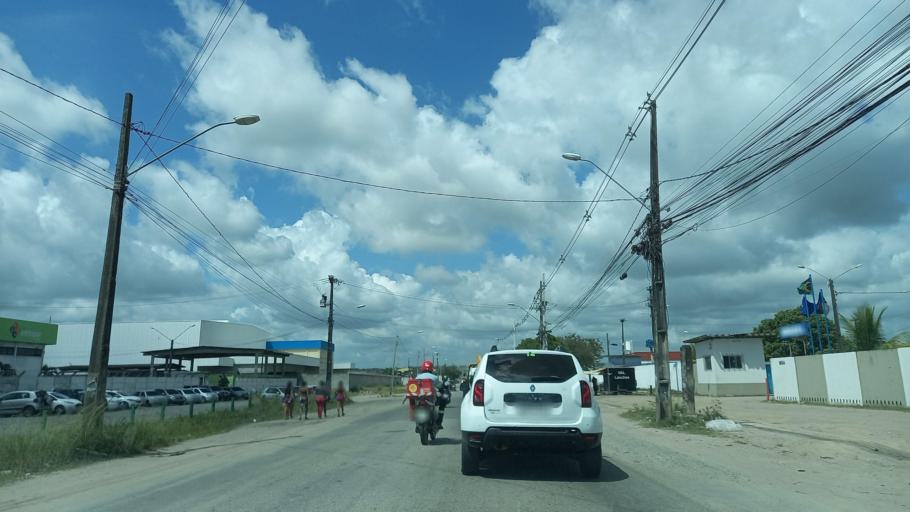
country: BR
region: Pernambuco
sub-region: Jaboatao Dos Guararapes
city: Jaboatao
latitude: -8.1557
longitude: -34.9647
